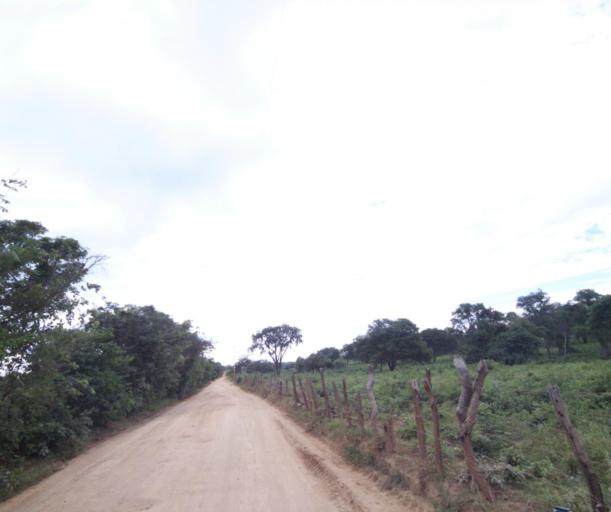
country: BR
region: Bahia
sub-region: Carinhanha
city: Carinhanha
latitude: -14.1842
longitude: -44.5016
